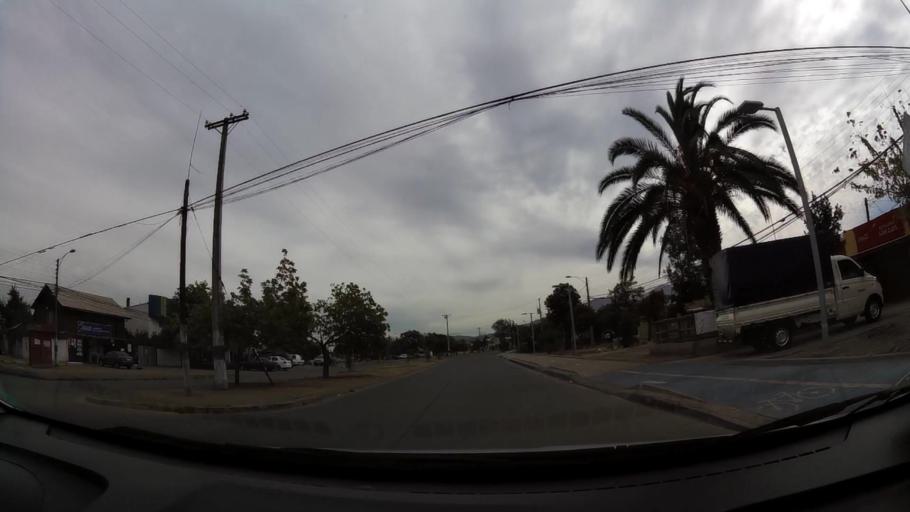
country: CL
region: O'Higgins
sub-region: Provincia de Cachapoal
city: Rancagua
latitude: -34.1459
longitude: -70.7339
